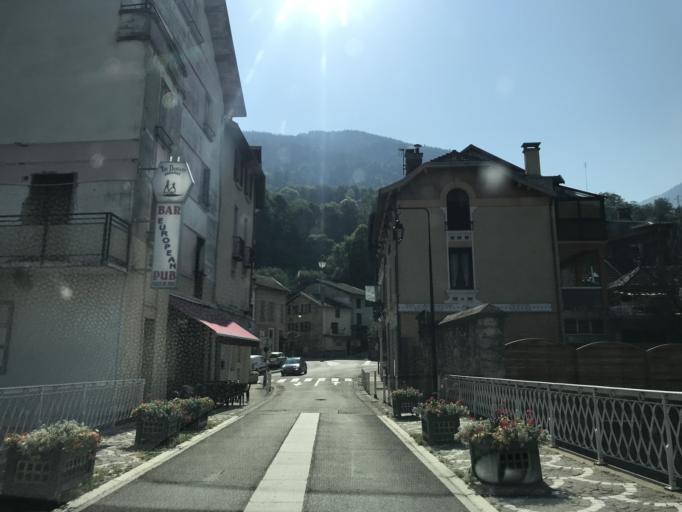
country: FR
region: Rhone-Alpes
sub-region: Departement de l'Isere
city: Allevard
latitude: 45.3935
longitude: 6.0752
